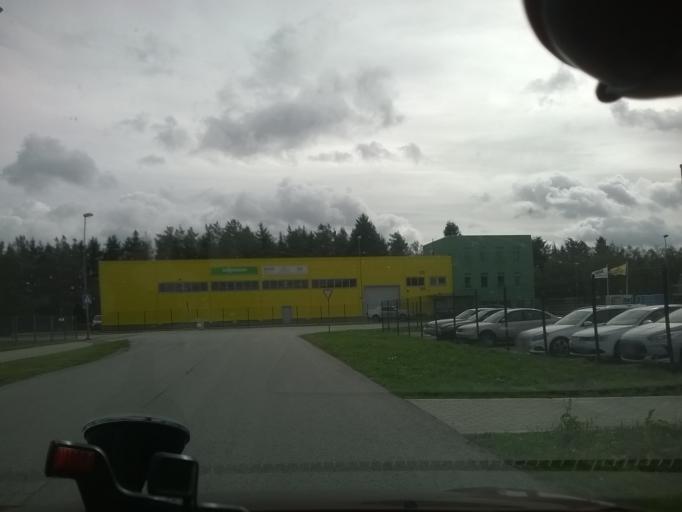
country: EE
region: Harju
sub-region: Rae vald
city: Jueri
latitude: 59.3854
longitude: 24.8273
